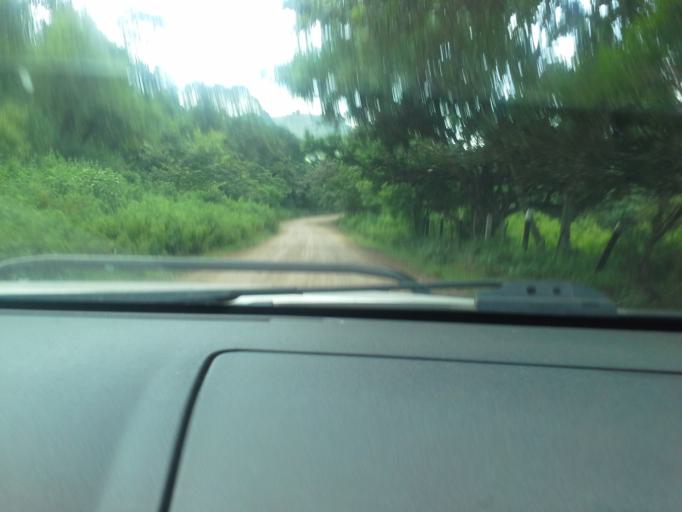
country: NI
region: Matagalpa
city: Terrabona
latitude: 12.7082
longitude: -85.9558
